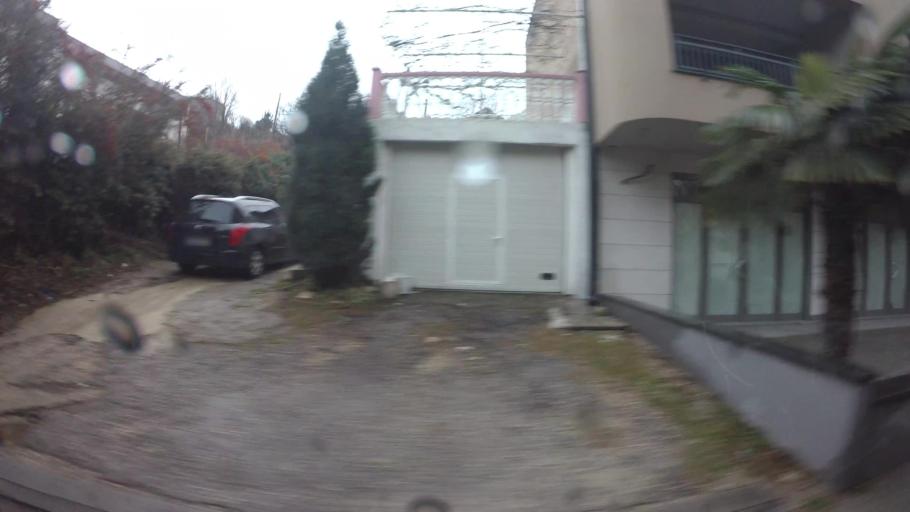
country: BA
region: Federation of Bosnia and Herzegovina
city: Cim
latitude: 43.3506
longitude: 17.7943
